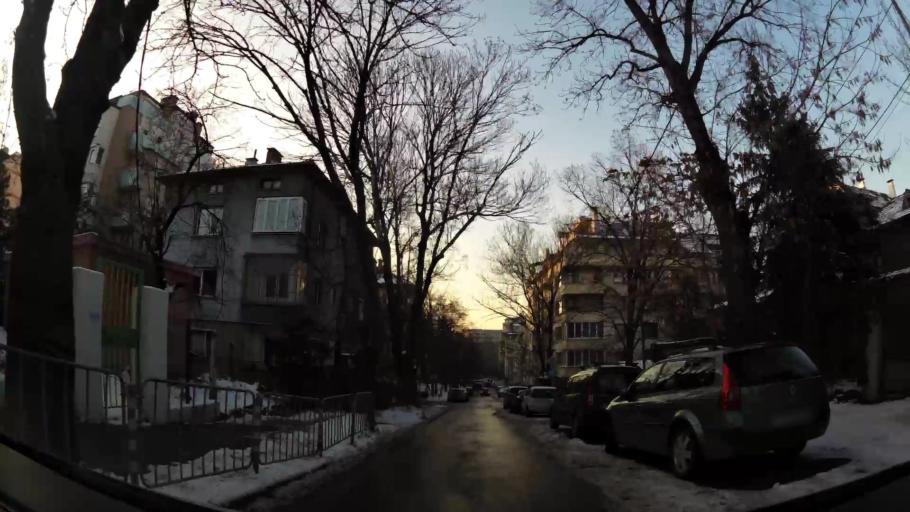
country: BG
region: Sofia-Capital
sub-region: Stolichna Obshtina
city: Sofia
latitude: 42.6916
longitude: 23.3573
